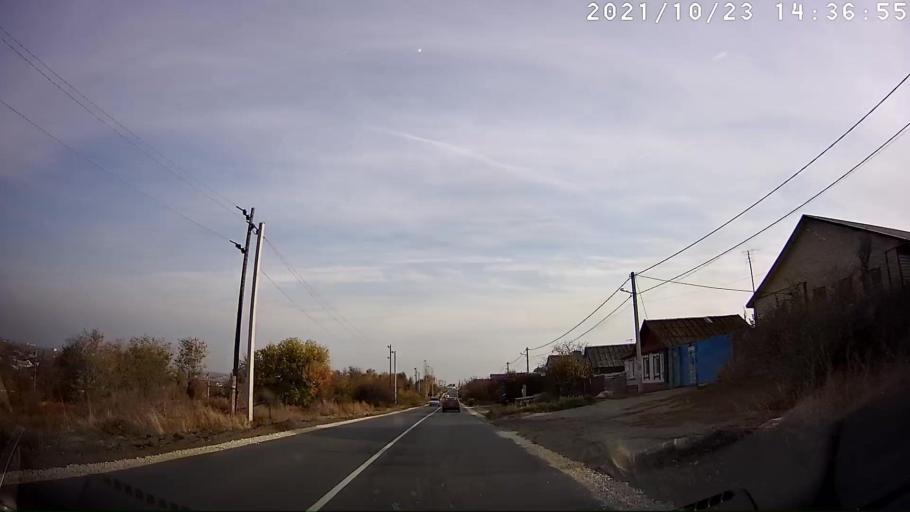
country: RU
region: Volgograd
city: Krasnoslobodsk
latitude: 48.5004
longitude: 44.5449
